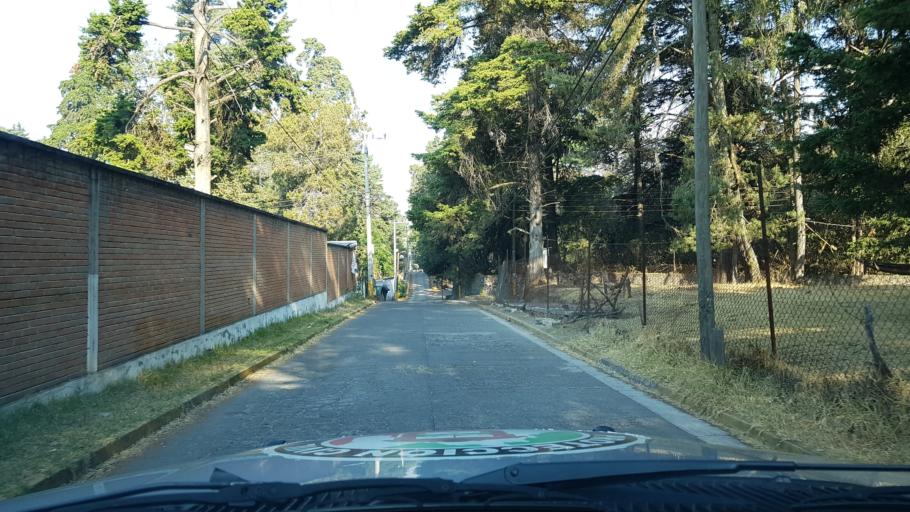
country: MX
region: Mexico
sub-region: Amecameca
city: San Diego Huehuecalco
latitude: 19.0725
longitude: -98.7790
